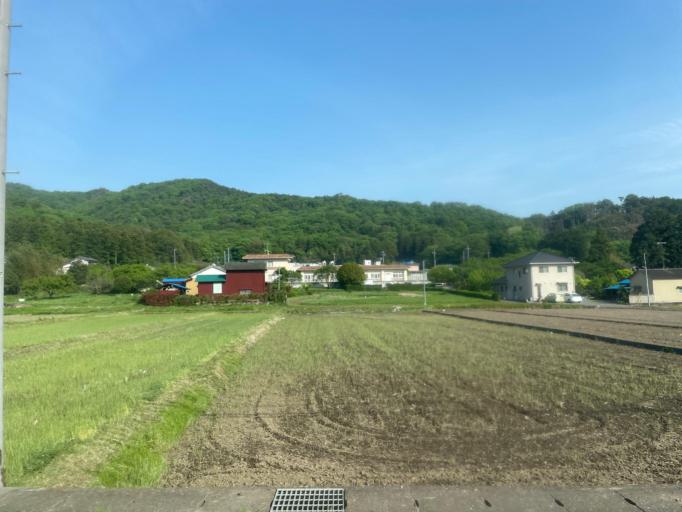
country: JP
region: Tochigi
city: Ashikaga
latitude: 36.3320
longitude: 139.5033
